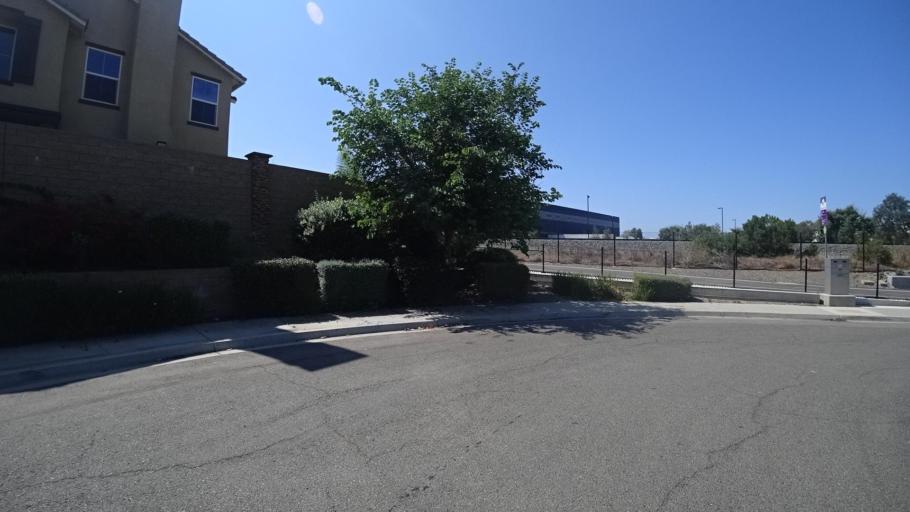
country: US
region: California
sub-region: San Diego County
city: Lake San Marcos
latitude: 33.1632
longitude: -117.1990
